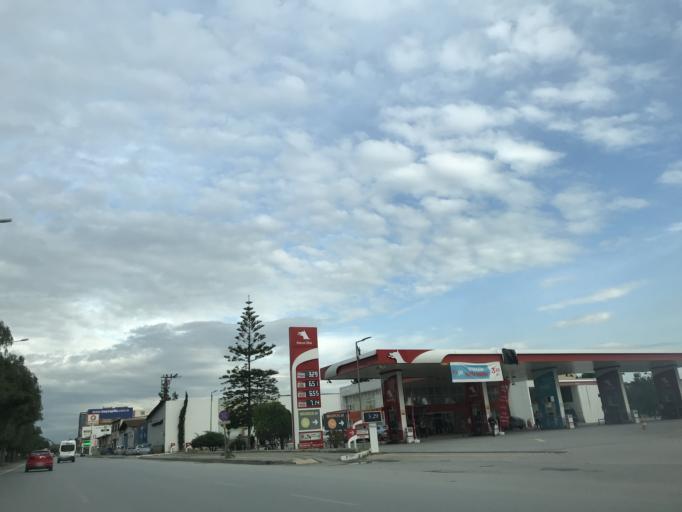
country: TR
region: Adana
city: Seyhan
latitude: 36.9946
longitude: 35.2820
